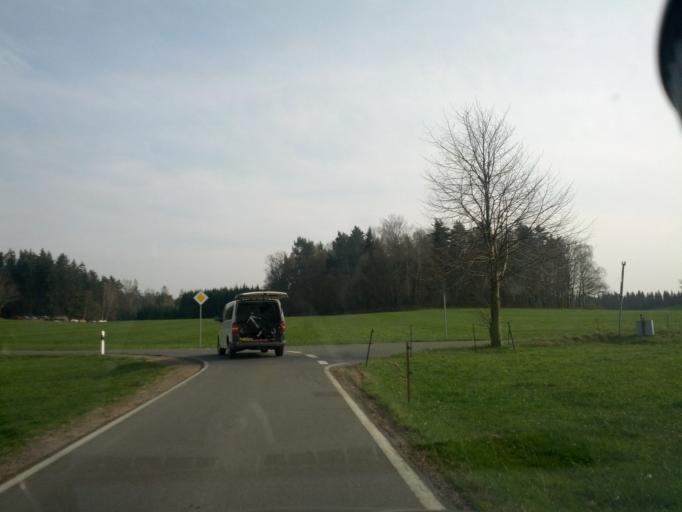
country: DE
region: Saxony
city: Kirchberg
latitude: 50.5810
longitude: 12.5149
